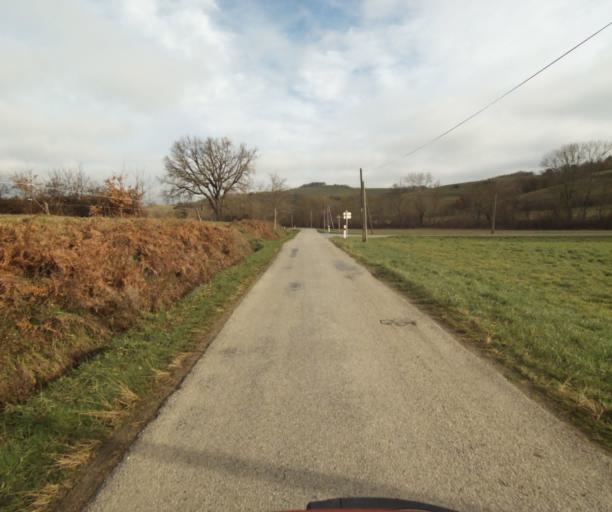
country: FR
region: Midi-Pyrenees
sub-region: Departement de l'Ariege
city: Saverdun
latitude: 43.1903
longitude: 1.5215
